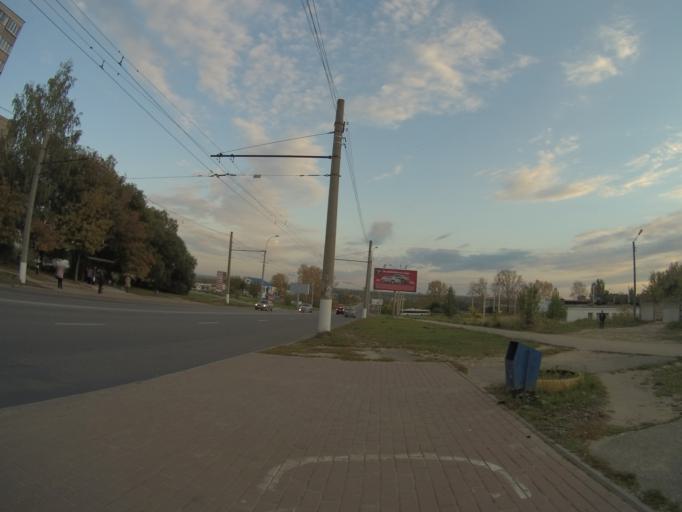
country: RU
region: Vladimir
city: Vladimir
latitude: 56.1023
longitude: 40.3471
